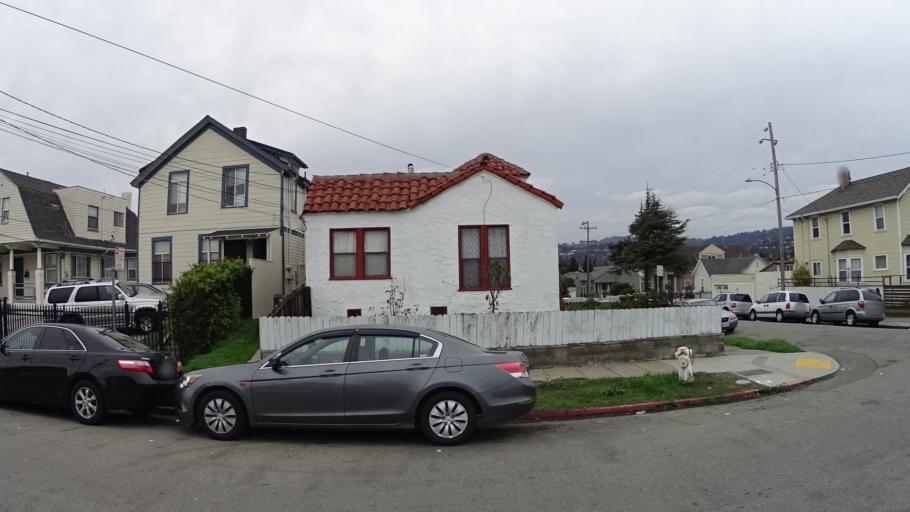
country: US
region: California
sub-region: Alameda County
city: Piedmont
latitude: 37.8000
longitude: -122.2313
